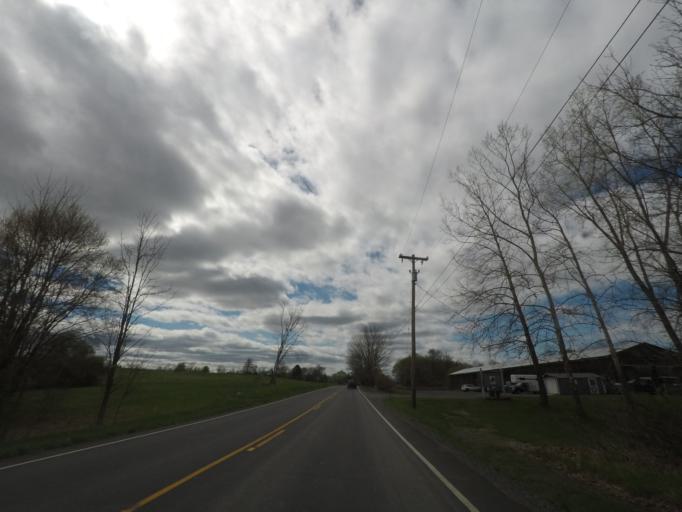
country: US
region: New York
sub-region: Columbia County
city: Valatie
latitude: 42.3957
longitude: -73.6468
